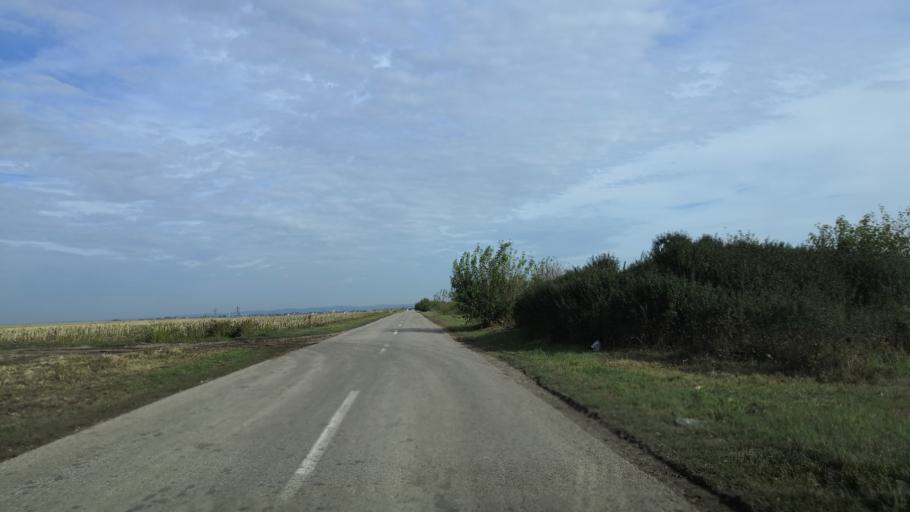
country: RS
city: Novi Karlovci
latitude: 45.0347
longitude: 20.1733
